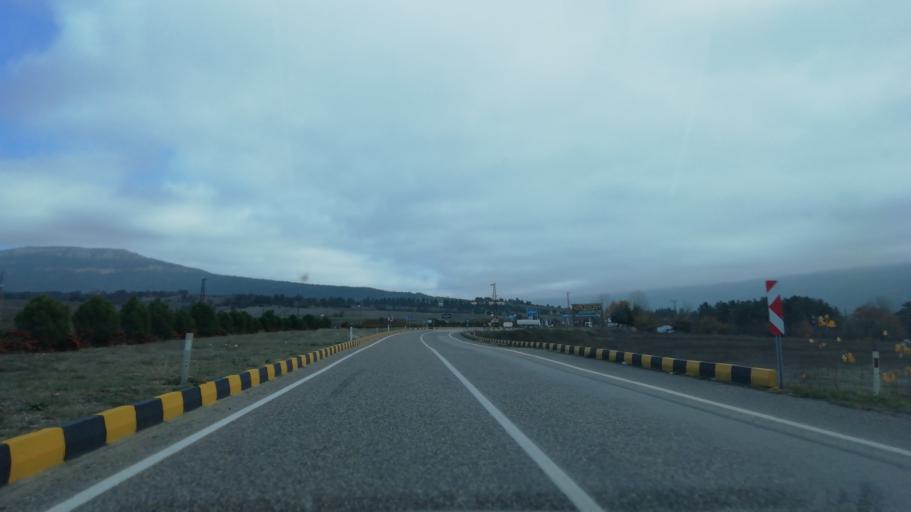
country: TR
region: Karabuk
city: Safranbolu
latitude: 41.2227
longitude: 32.7802
